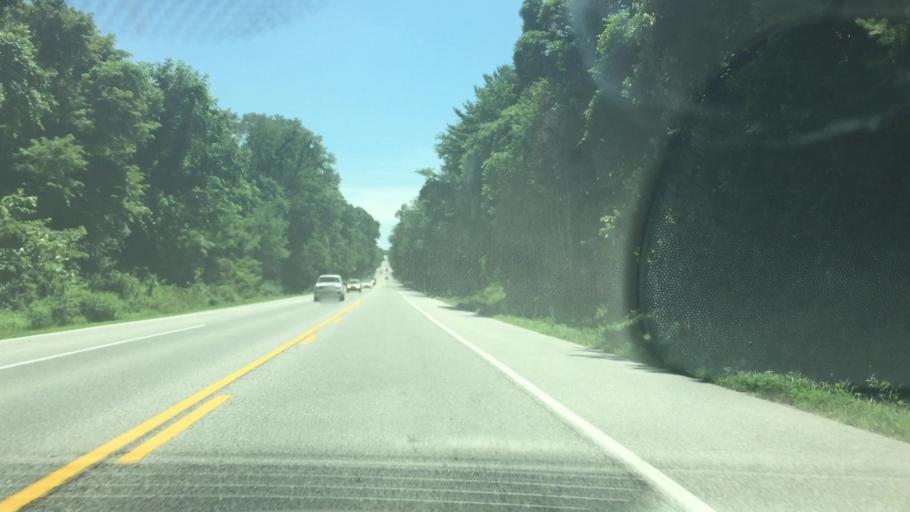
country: US
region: Maryland
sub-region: Cecil County
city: Rising Sun
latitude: 39.6626
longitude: -76.0757
